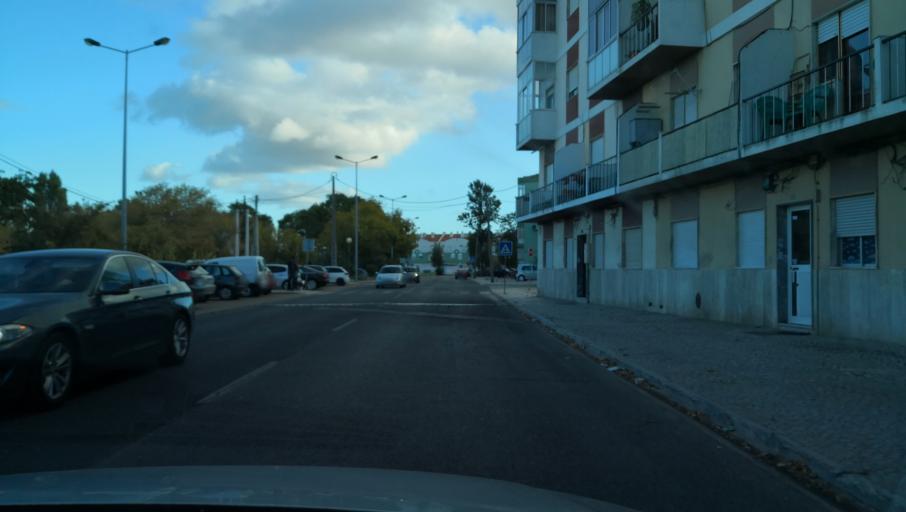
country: PT
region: Setubal
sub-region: Moita
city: Alhos Vedros
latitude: 38.6632
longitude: -9.0437
